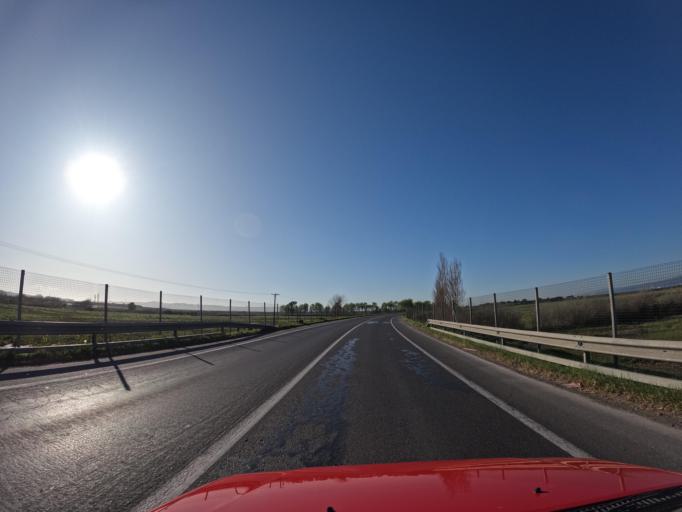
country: CL
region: Biobio
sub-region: Provincia de Concepcion
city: Penco
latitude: -36.7634
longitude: -73.0495
